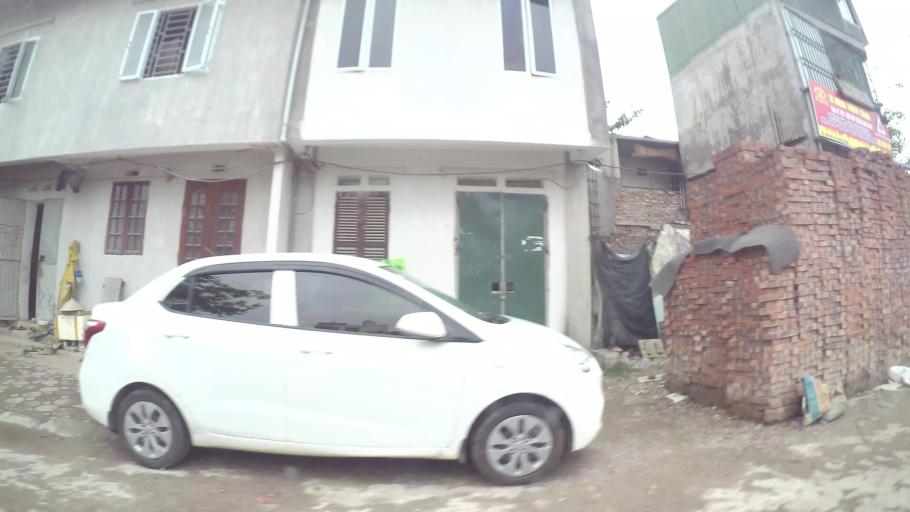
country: VN
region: Ha Noi
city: Van Dien
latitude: 20.9750
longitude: 105.8504
